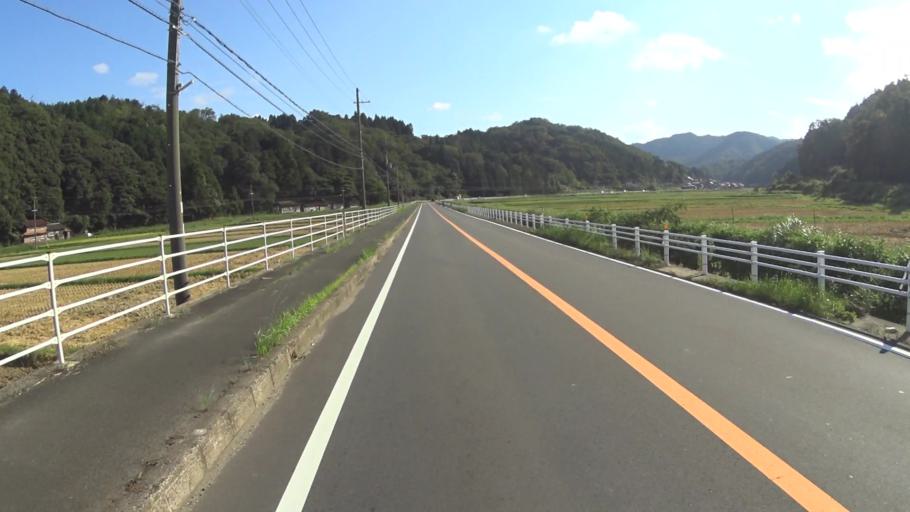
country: JP
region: Kyoto
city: Miyazu
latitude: 35.6655
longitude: 135.0236
